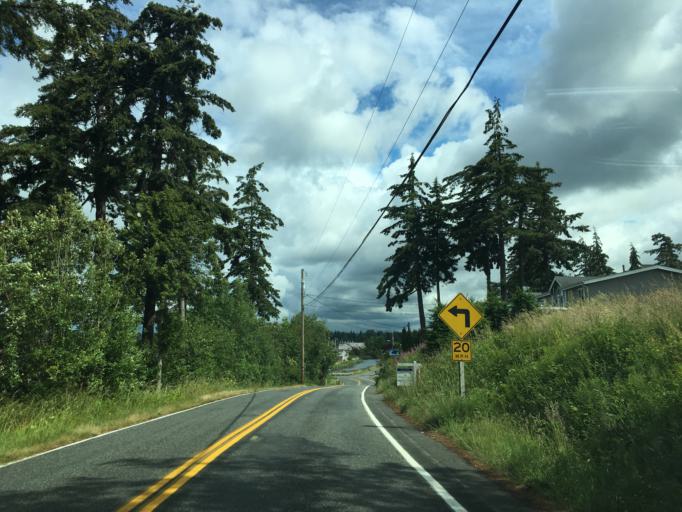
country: US
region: Washington
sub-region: Whatcom County
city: Birch Bay
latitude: 48.9113
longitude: -122.7484
